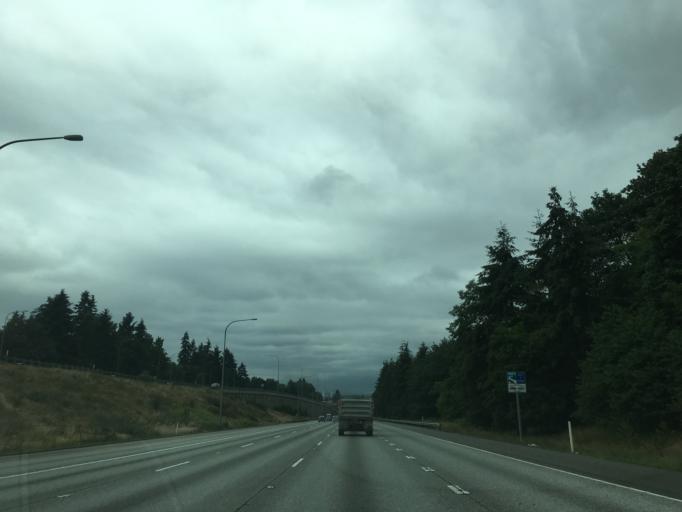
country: US
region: Washington
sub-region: Snohomish County
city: Everett
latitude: 47.9506
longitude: -122.1989
